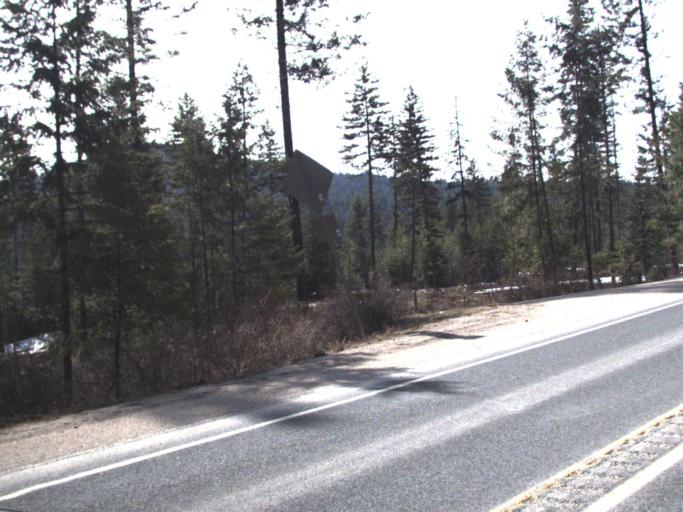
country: US
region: Washington
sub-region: Stevens County
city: Chewelah
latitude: 48.5080
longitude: -117.6640
